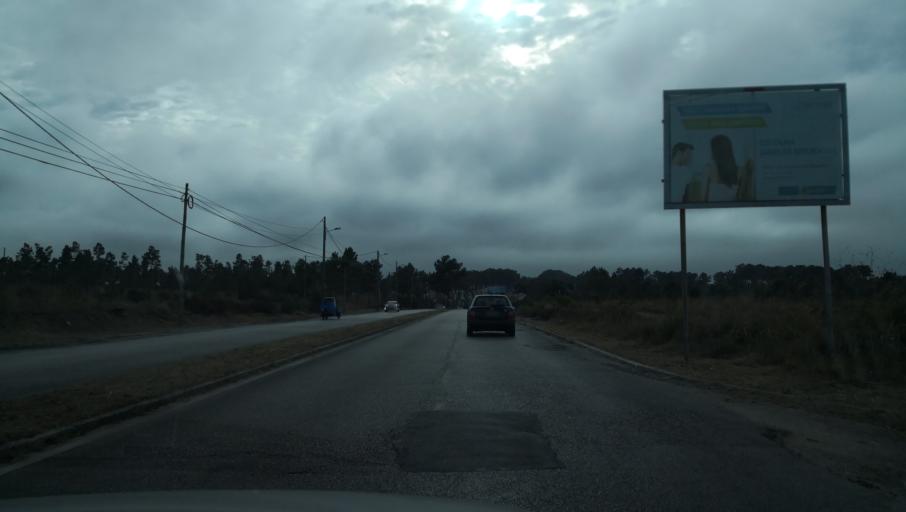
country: PT
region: Setubal
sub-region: Seixal
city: Amora
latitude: 38.5939
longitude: -9.1475
